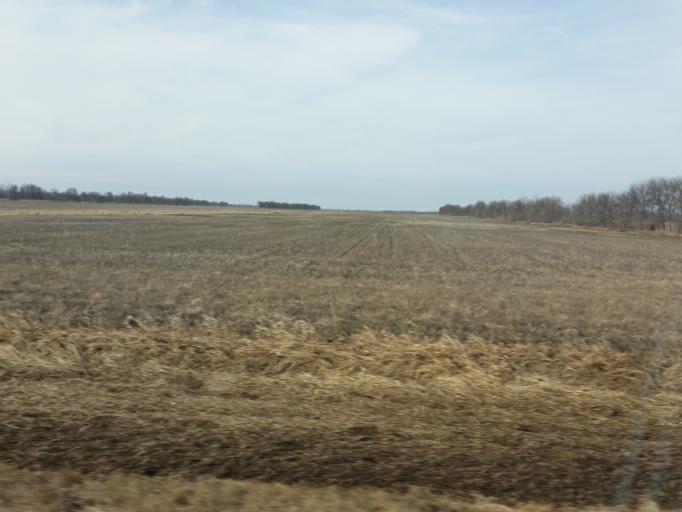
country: US
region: Minnesota
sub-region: Wilkin County
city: Breckenridge
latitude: 46.4712
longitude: -96.5750
